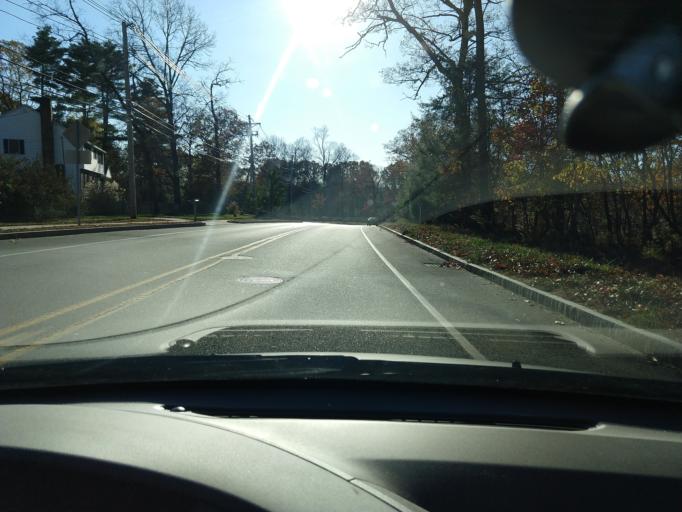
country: US
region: Massachusetts
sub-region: Middlesex County
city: Billerica
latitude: 42.5498
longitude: -71.2742
